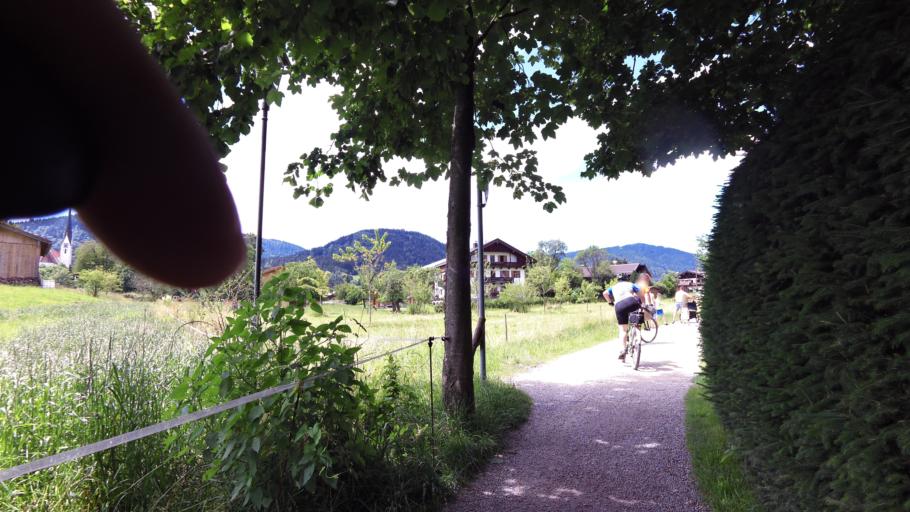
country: DE
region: Bavaria
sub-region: Upper Bavaria
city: Bad Wiessee
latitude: 47.7074
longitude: 11.7331
